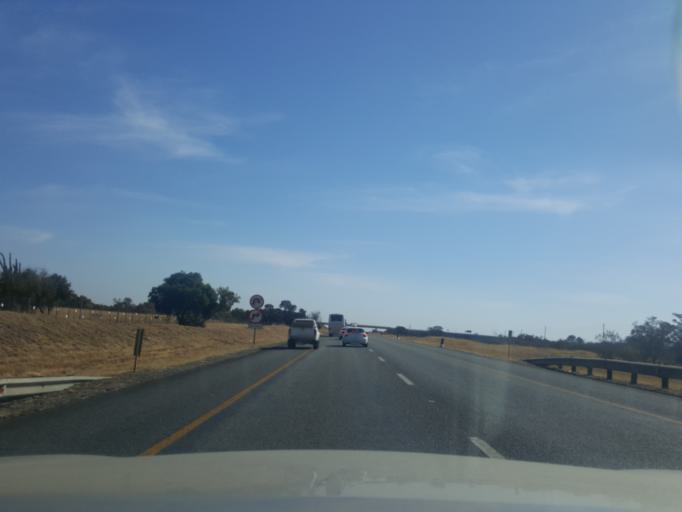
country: ZA
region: North-West
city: Ga-Rankuwa
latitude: -25.6499
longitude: 27.9547
